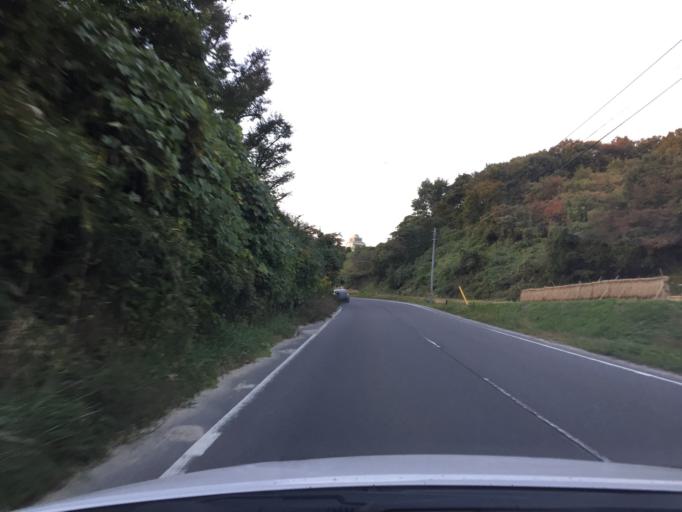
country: JP
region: Fukushima
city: Miharu
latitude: 37.3818
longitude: 140.4498
